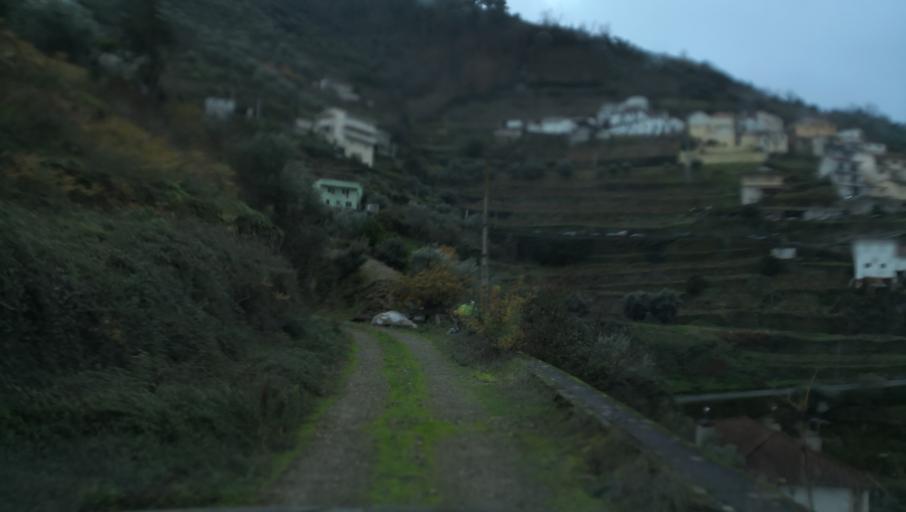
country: PT
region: Vila Real
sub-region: Santa Marta de Penaguiao
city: Santa Marta de Penaguiao
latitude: 41.2244
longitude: -7.7498
